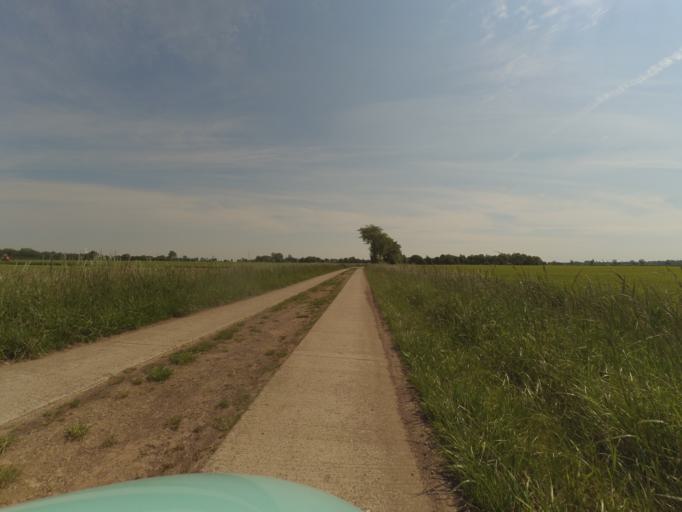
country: DE
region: Lower Saxony
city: Hohenhameln
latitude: 52.2694
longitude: 10.0334
